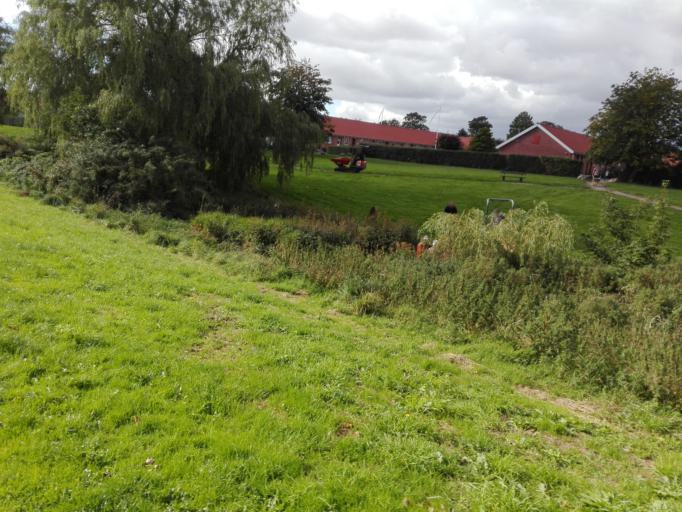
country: DK
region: Central Jutland
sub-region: Arhus Kommune
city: Beder
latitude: 56.0625
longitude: 10.2089
